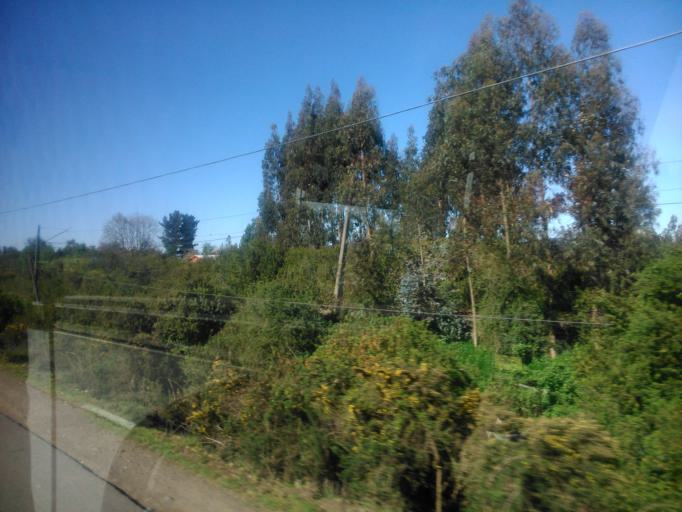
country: CL
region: Araucania
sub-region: Provincia de Cautin
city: Temuco
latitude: -38.7920
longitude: -72.6182
